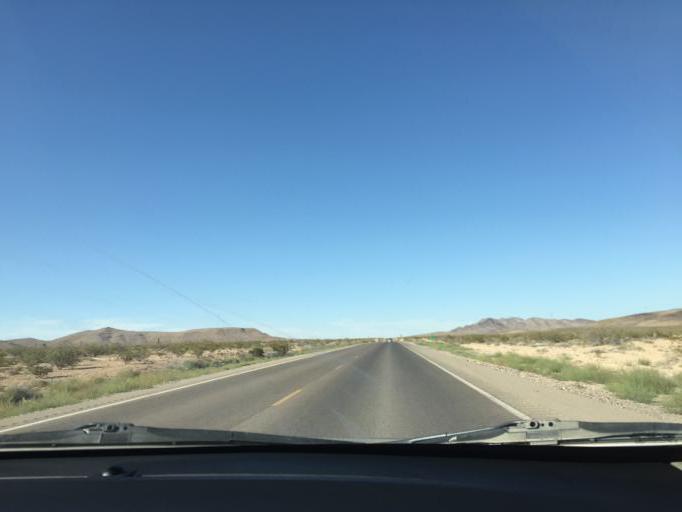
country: US
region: Nevada
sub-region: Clark County
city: Enterprise
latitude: 35.8461
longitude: -115.2652
